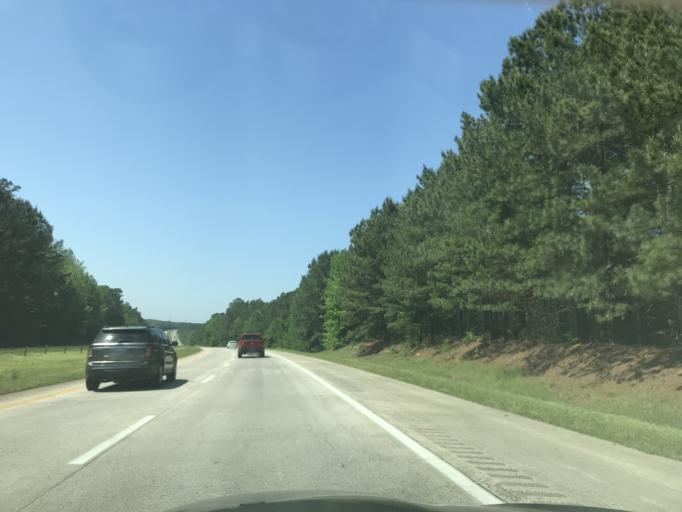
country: US
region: North Carolina
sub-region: Johnston County
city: Benson
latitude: 35.4531
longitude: -78.5342
